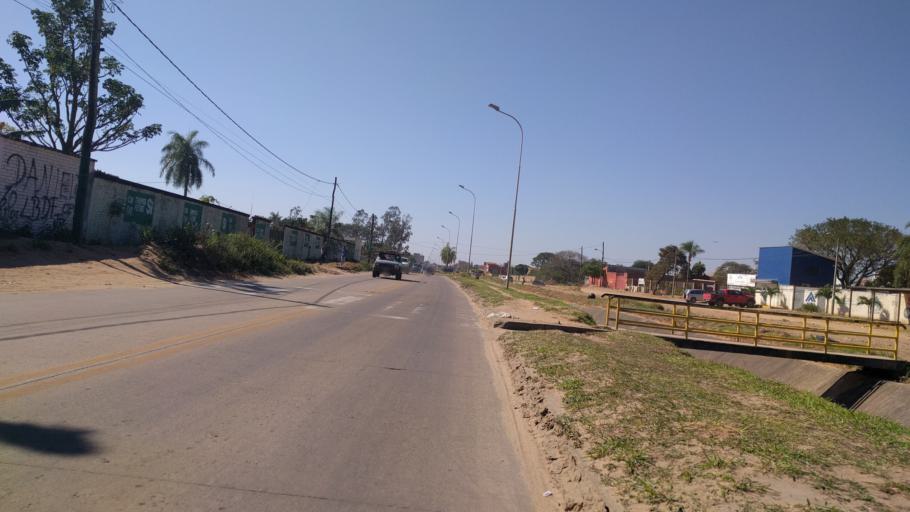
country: BO
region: Santa Cruz
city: Santa Cruz de la Sierra
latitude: -17.8426
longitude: -63.1914
